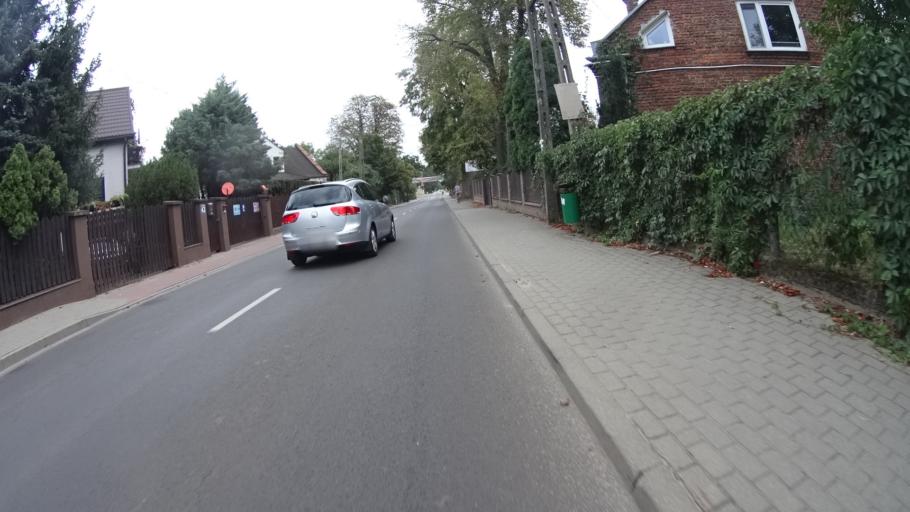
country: PL
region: Masovian Voivodeship
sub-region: Powiat pruszkowski
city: Granica
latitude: 52.1417
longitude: 20.7936
